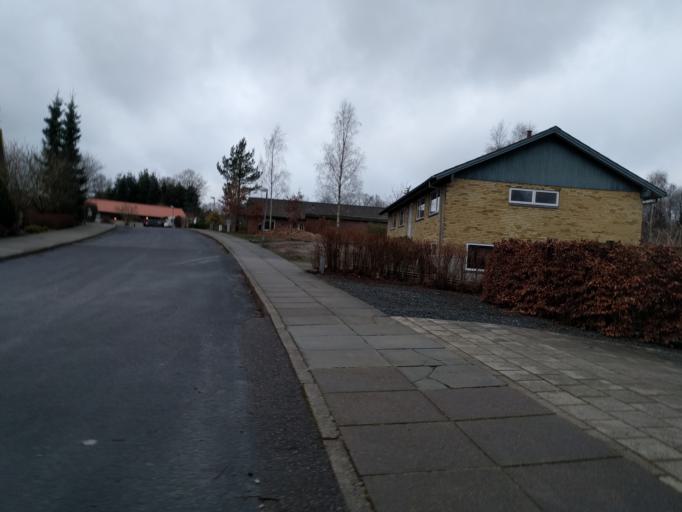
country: DK
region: Central Jutland
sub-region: Silkeborg Kommune
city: Silkeborg
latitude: 56.1855
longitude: 9.5304
